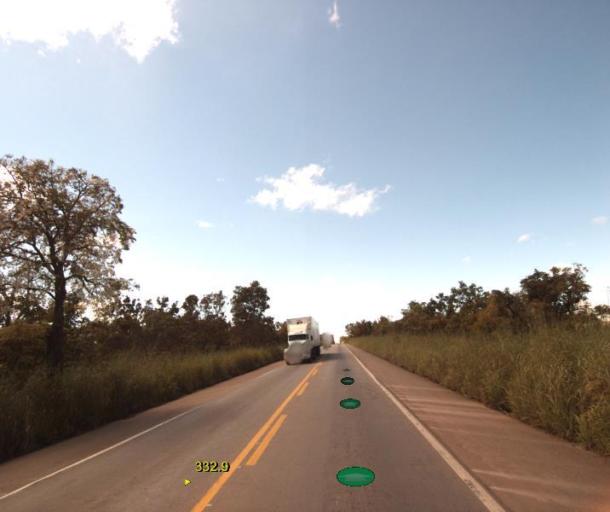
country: BR
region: Goias
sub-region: Uruana
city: Uruana
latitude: -15.5349
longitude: -49.4463
